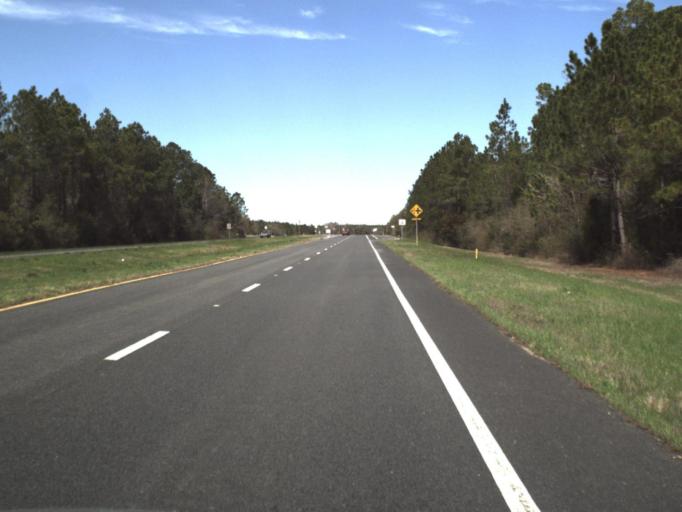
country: US
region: Florida
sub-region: Washington County
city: Chipley
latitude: 30.5957
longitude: -85.3961
